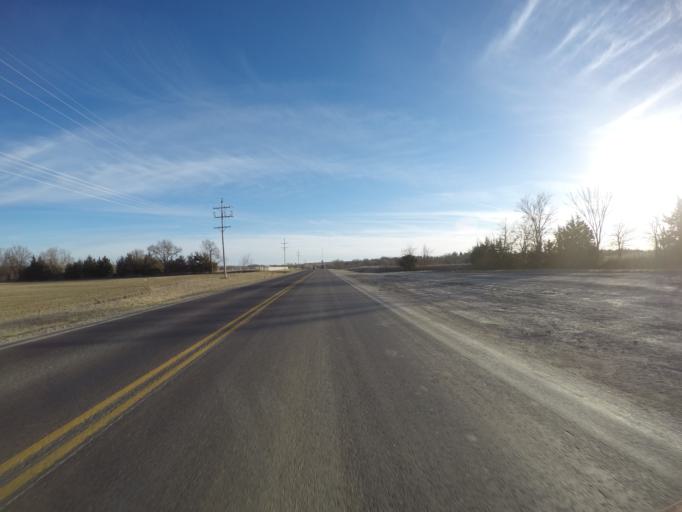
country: US
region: Kansas
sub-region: Marshall County
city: Marysville
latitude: 39.8492
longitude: -96.6667
